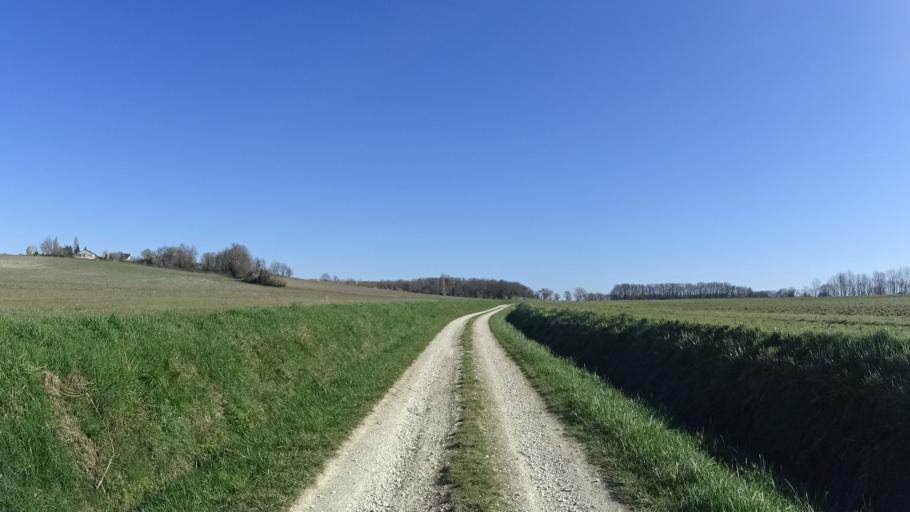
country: FR
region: Aquitaine
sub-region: Departement de la Dordogne
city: Saint-Aulaye
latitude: 45.2184
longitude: 0.1131
